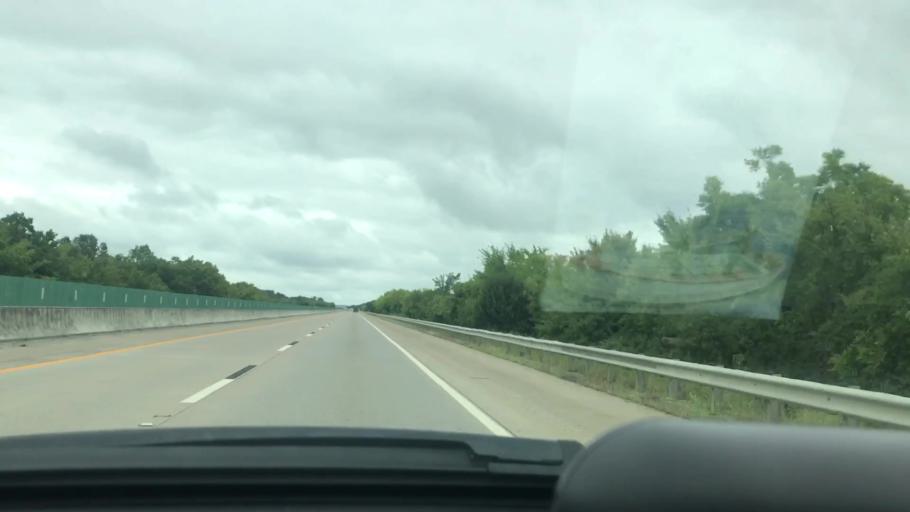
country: US
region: Oklahoma
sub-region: Pittsburg County
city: Krebs
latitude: 35.0208
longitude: -95.7167
